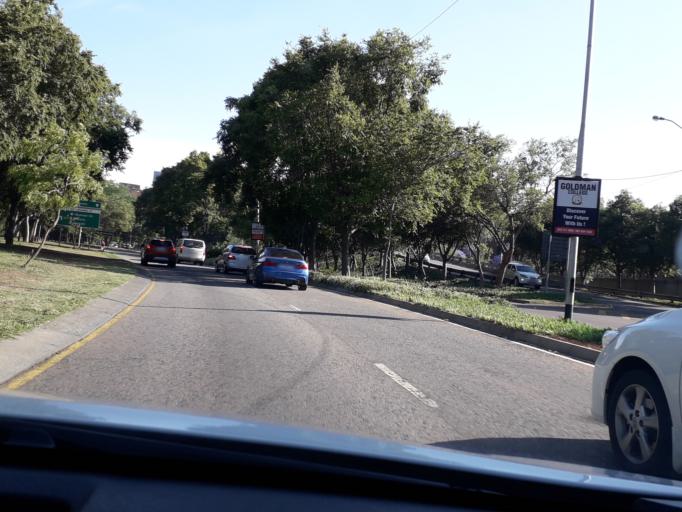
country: ZA
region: Gauteng
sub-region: City of Tshwane Metropolitan Municipality
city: Pretoria
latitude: -25.7589
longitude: 28.1959
